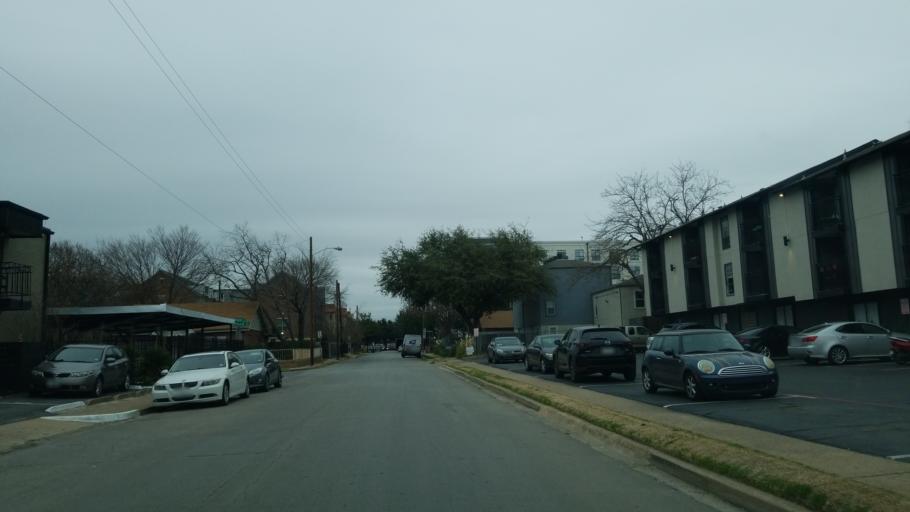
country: US
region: Texas
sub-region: Dallas County
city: Dallas
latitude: 32.8109
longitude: -96.8153
